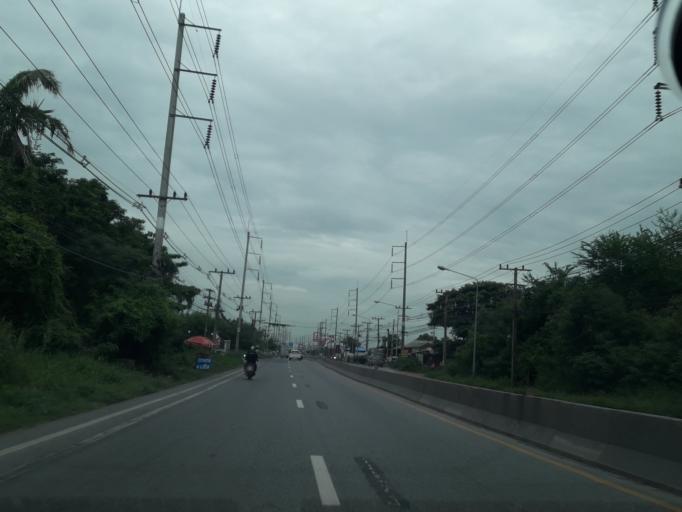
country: TH
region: Pathum Thani
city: Lam Luk Ka
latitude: 13.9396
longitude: 100.7607
